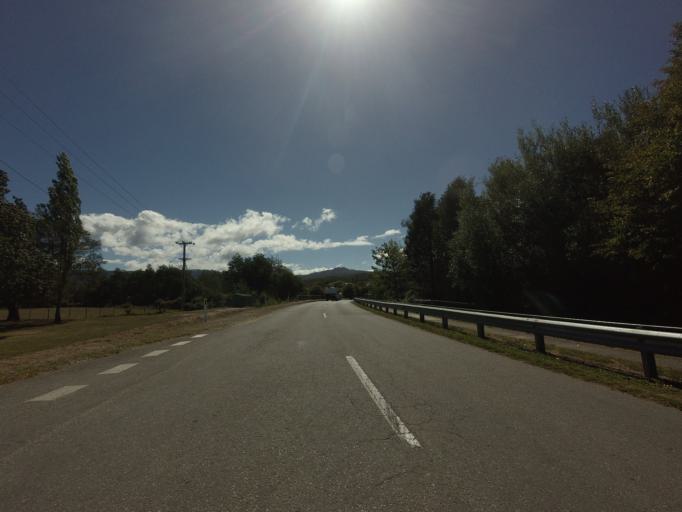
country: AU
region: Tasmania
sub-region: Break O'Day
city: St Helens
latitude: -41.5831
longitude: 148.1855
